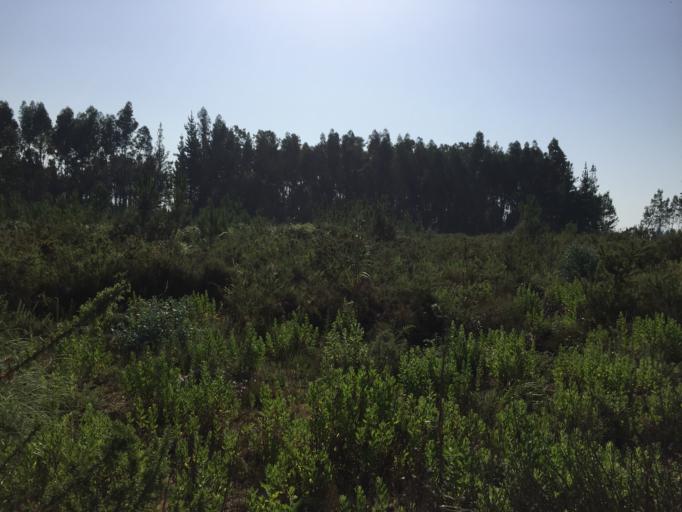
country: PT
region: Coimbra
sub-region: Cantanhede
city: Cantanhede
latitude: 40.4222
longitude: -8.5428
